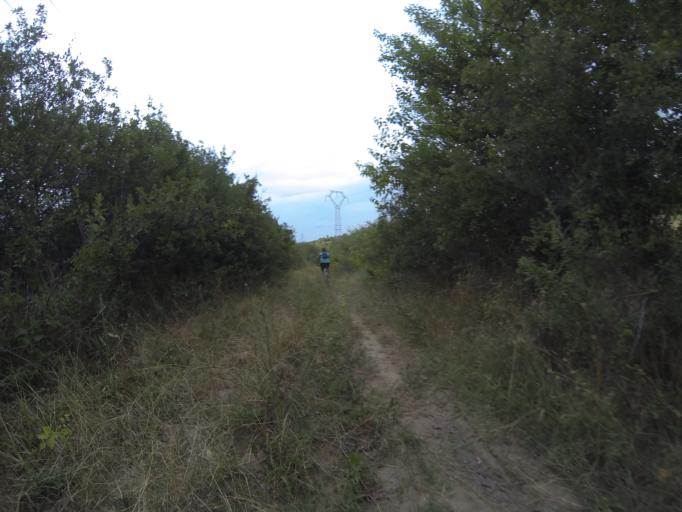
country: RO
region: Dolj
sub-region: Comuna Cotofenii din Fata
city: Cotofenii din Fata
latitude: 44.4808
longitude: 23.6875
